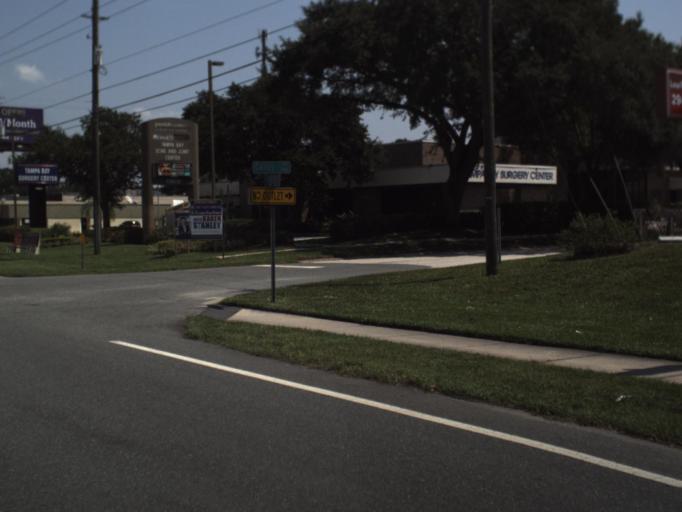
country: US
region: Florida
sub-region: Hillsborough County
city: Carrollwood
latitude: 28.0559
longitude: -82.5038
